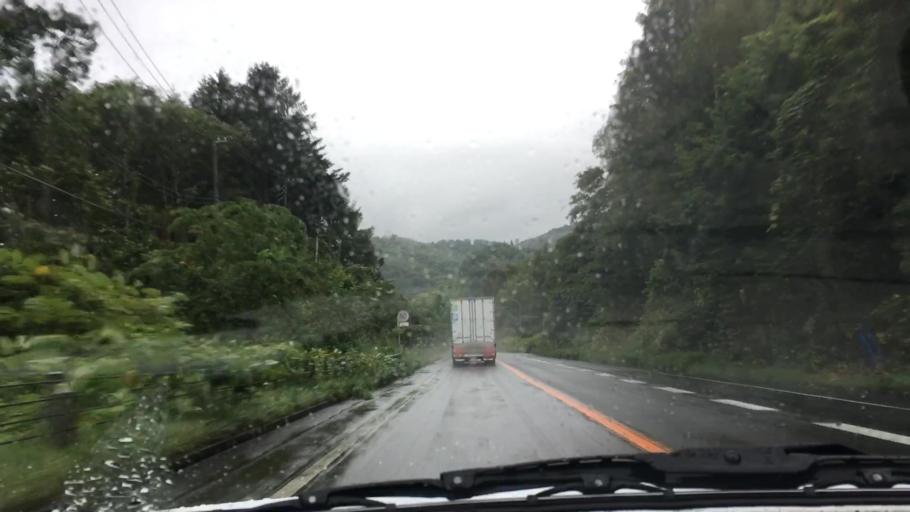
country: JP
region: Hokkaido
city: Niseko Town
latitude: 42.5992
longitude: 140.6647
